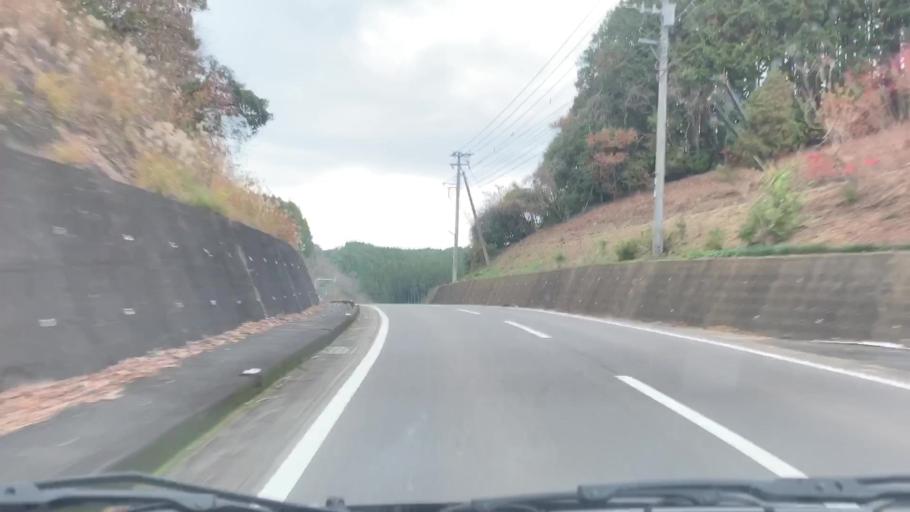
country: JP
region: Saga Prefecture
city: Ureshinomachi-shimojuku
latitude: 33.1305
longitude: 129.9764
